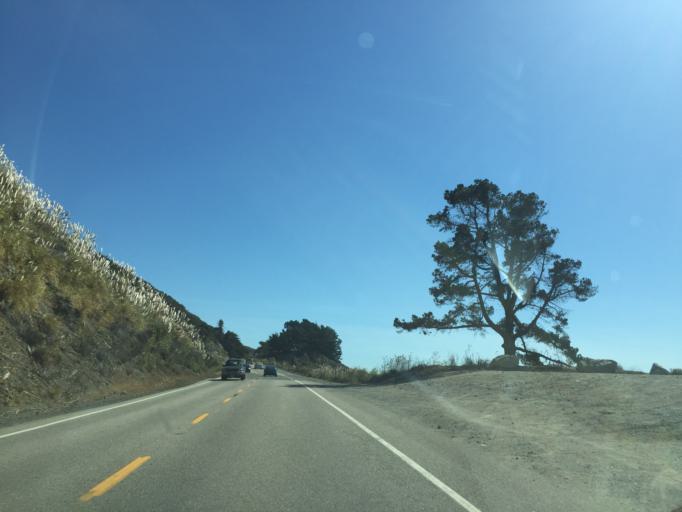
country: US
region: California
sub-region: Monterey County
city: Greenfield
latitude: 36.0327
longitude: -121.5764
